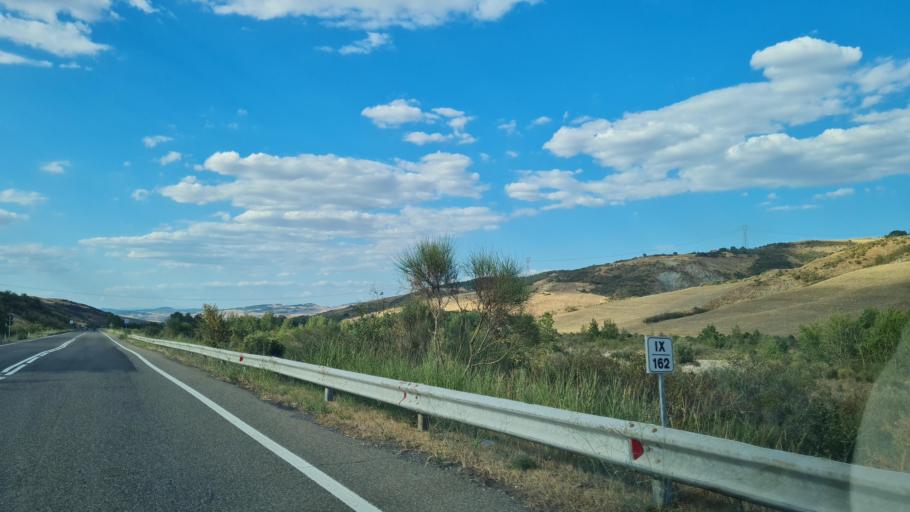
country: IT
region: Tuscany
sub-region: Provincia di Siena
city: Abbadia San Salvatore
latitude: 42.9520
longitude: 11.7076
